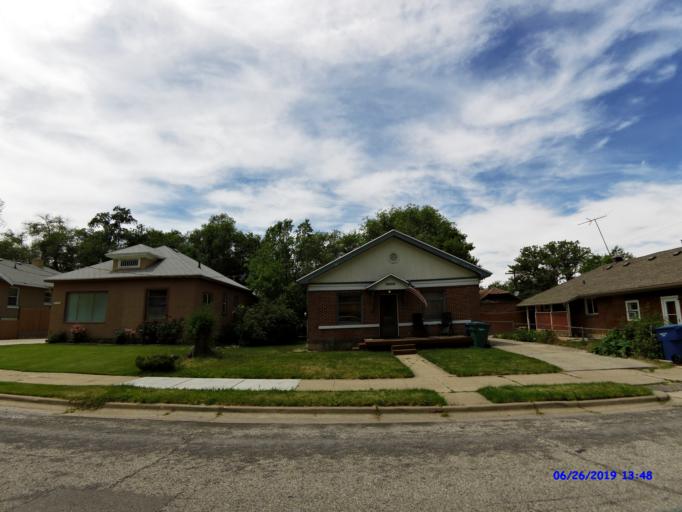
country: US
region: Utah
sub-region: Weber County
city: South Ogden
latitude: 41.1995
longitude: -111.9682
